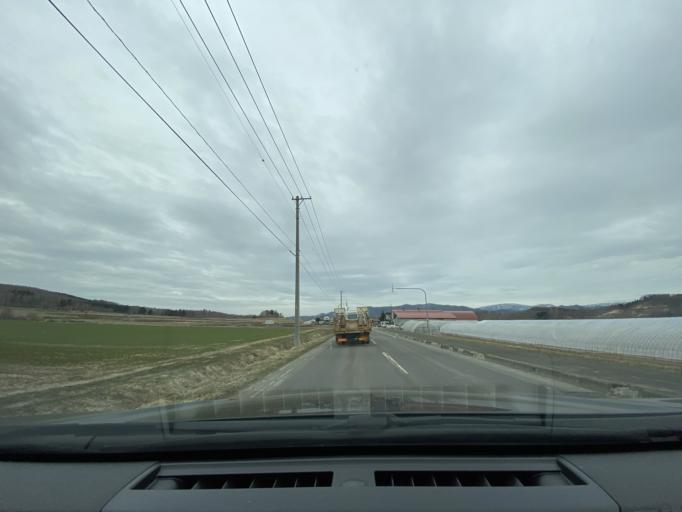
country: JP
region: Hokkaido
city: Nayoro
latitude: 44.0969
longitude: 142.4745
